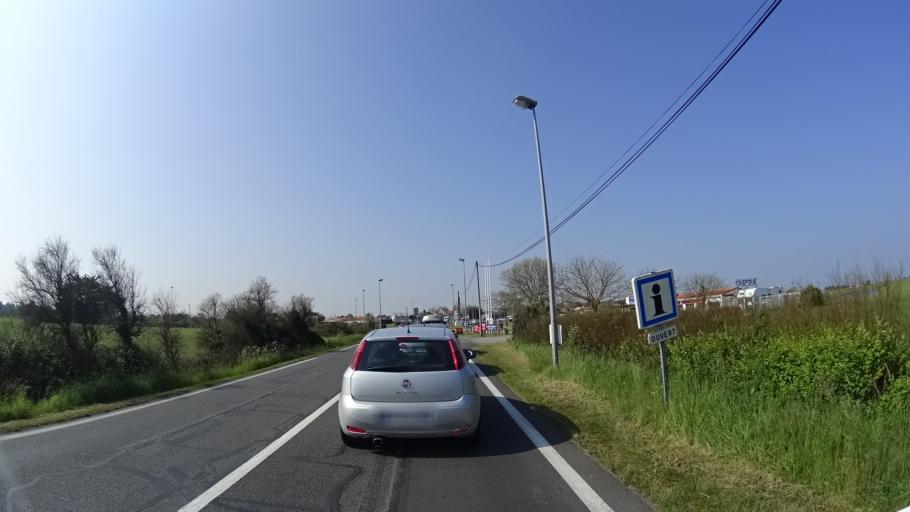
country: FR
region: Pays de la Loire
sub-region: Departement de la Vendee
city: Bouin
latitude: 46.9783
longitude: -1.9877
